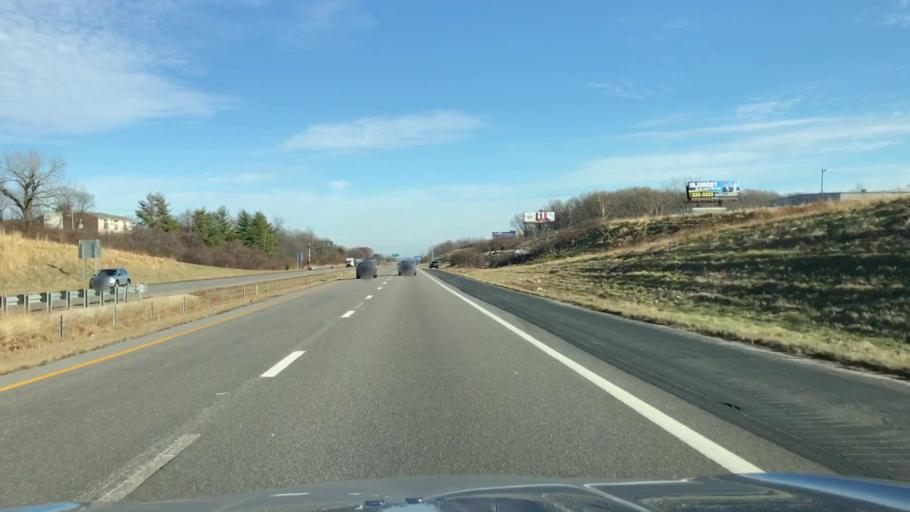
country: US
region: Missouri
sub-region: Saint Louis County
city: Glasgow Village
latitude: 38.7672
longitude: -90.2025
